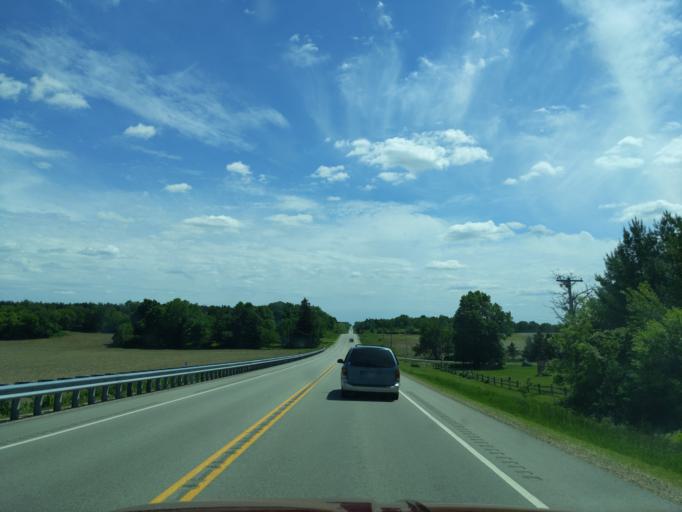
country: US
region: Wisconsin
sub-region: Columbia County
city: Poynette
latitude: 43.4222
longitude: -89.3280
